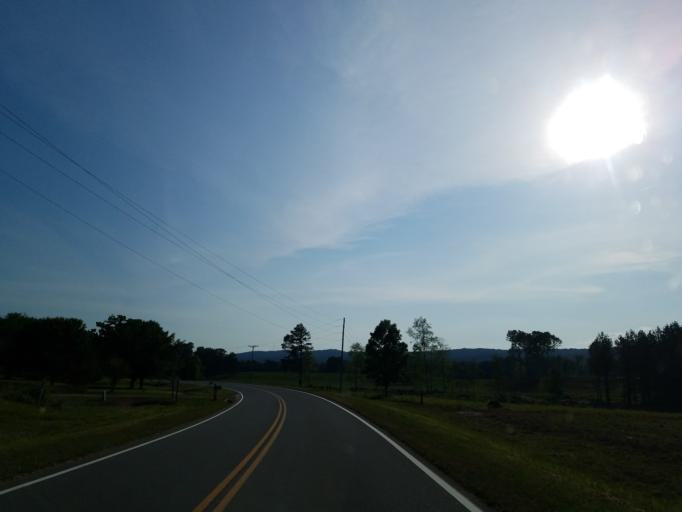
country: US
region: Georgia
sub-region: Chattooga County
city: Trion
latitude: 34.5097
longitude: -85.2371
